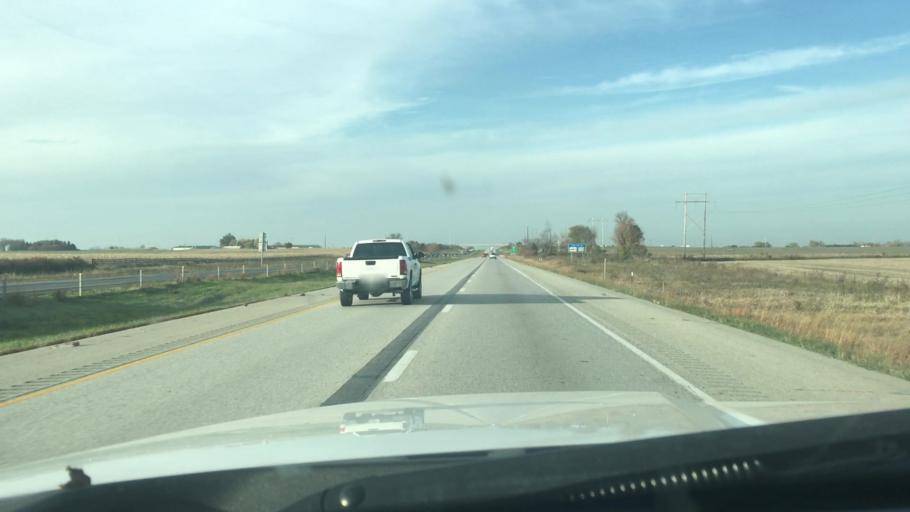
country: US
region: Iowa
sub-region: Story County
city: Huxley
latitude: 41.8667
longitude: -93.5712
